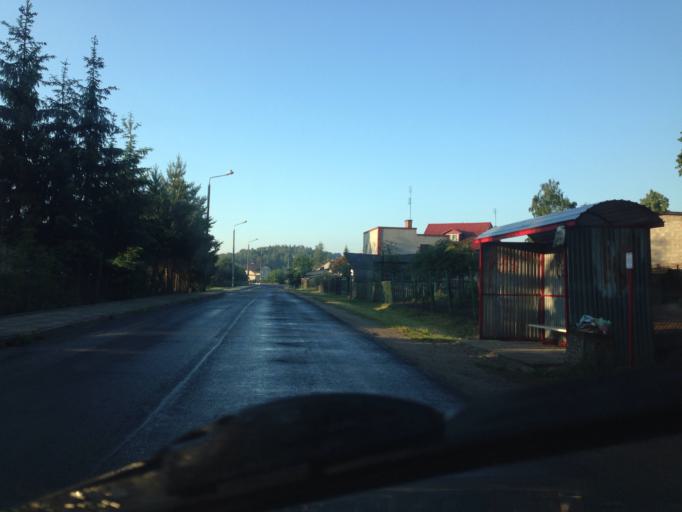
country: PL
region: Pomeranian Voivodeship
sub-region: Powiat tczewski
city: Gniew
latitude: 53.8246
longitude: 18.8159
